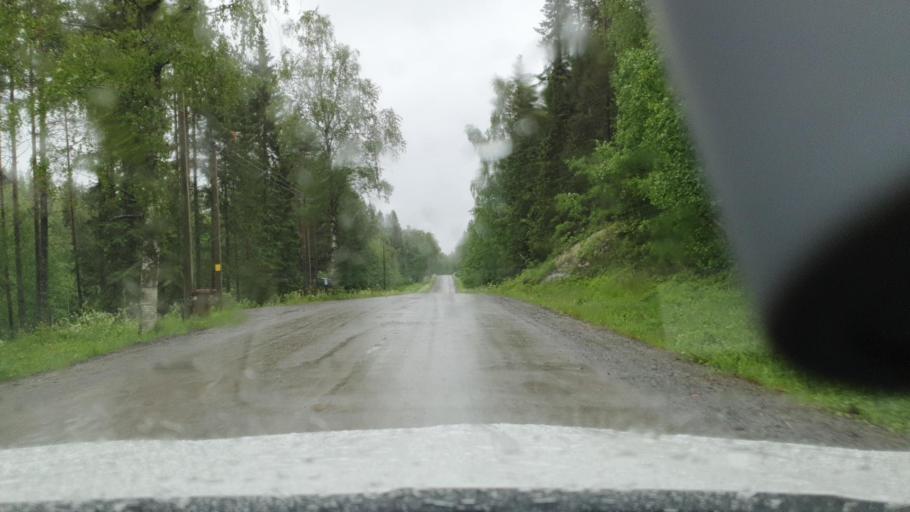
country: SE
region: Vaesterbotten
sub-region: Skelleftea Kommun
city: Burtraesk
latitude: 64.3532
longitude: 20.4798
